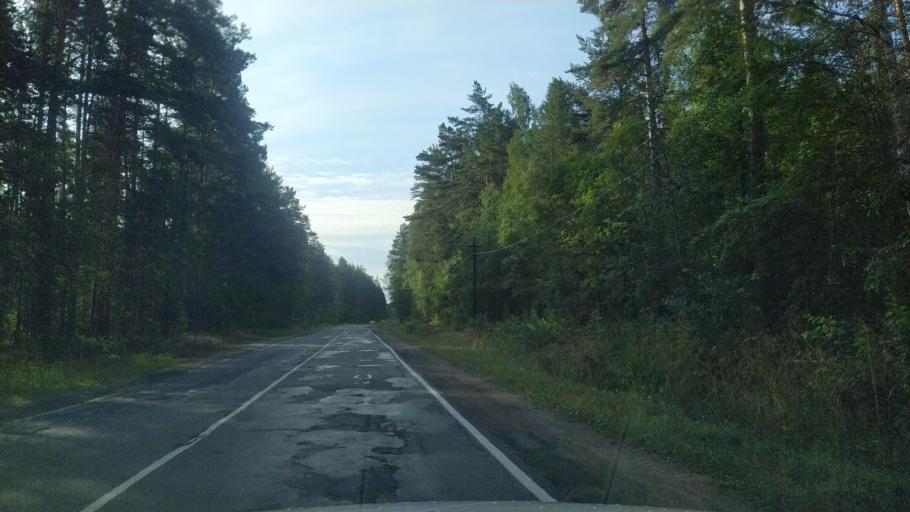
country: RU
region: Leningrad
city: Priozersk
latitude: 60.9993
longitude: 30.2455
